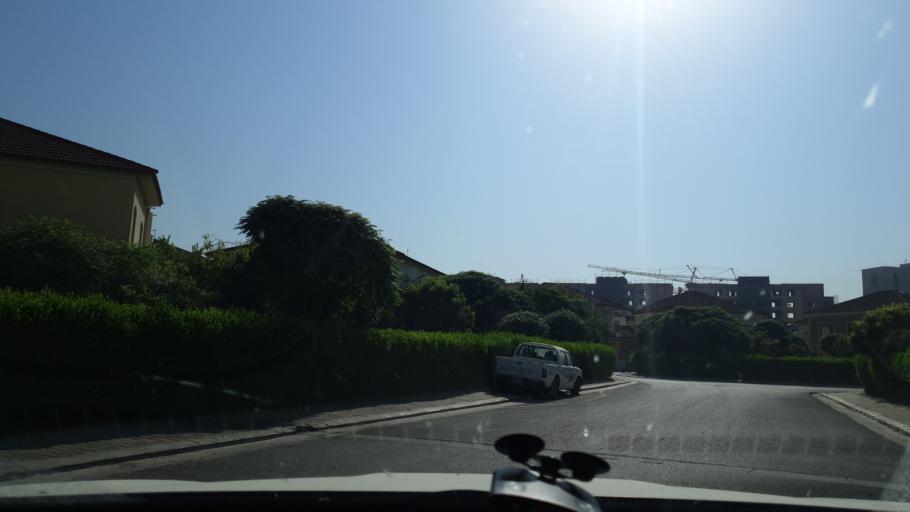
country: IQ
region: Arbil
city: Erbil
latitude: 36.1890
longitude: 43.9703
